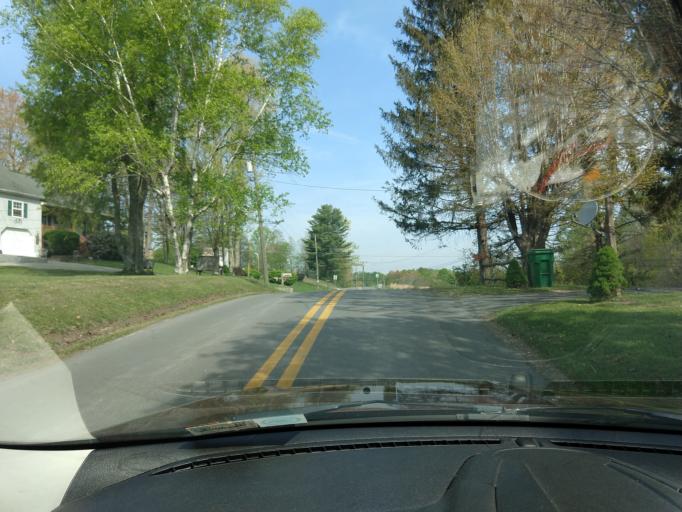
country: US
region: West Virginia
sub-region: Raleigh County
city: Crab Orchard
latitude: 37.7486
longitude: -81.2384
